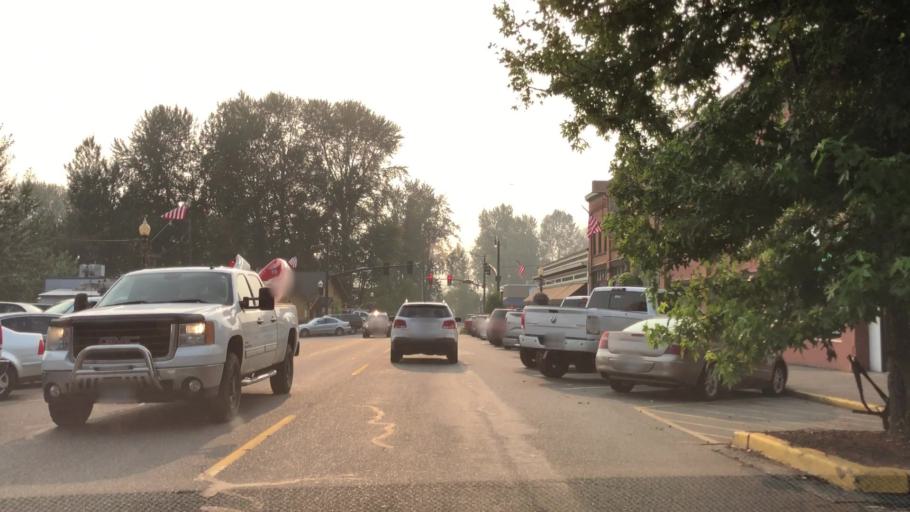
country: US
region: Washington
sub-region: Snohomish County
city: Snohomish
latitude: 47.9114
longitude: -122.0974
